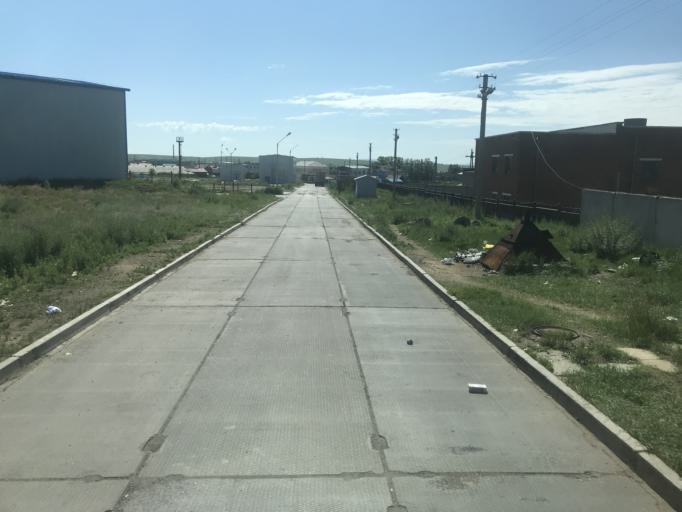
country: MN
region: Selenge
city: Altanbulag
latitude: 50.3217
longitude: 106.4875
